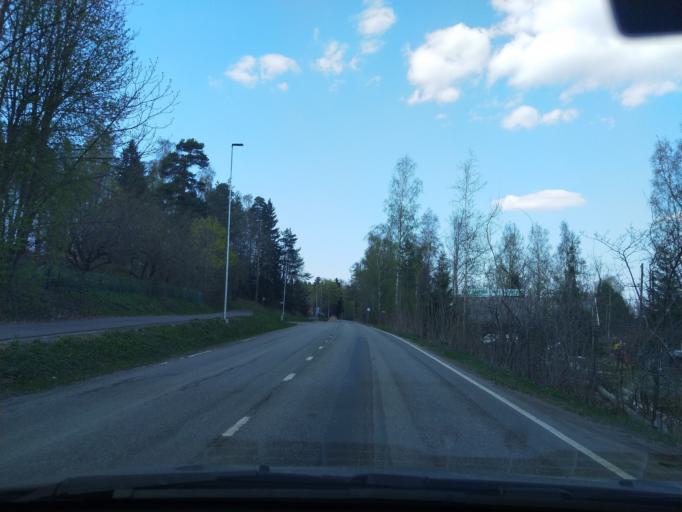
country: FI
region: Uusimaa
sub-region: Helsinki
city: Lohja
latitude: 60.2061
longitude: 24.0102
